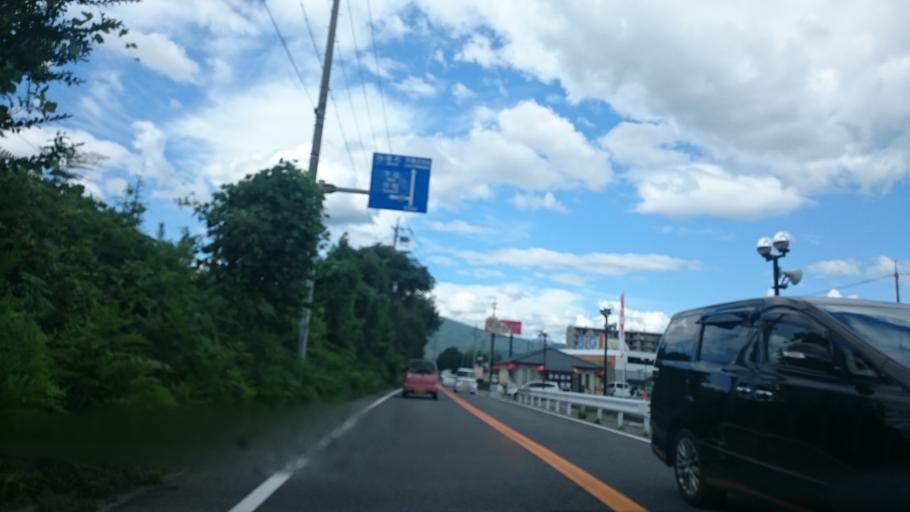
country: JP
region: Gifu
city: Nakatsugawa
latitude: 35.4890
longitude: 137.4880
